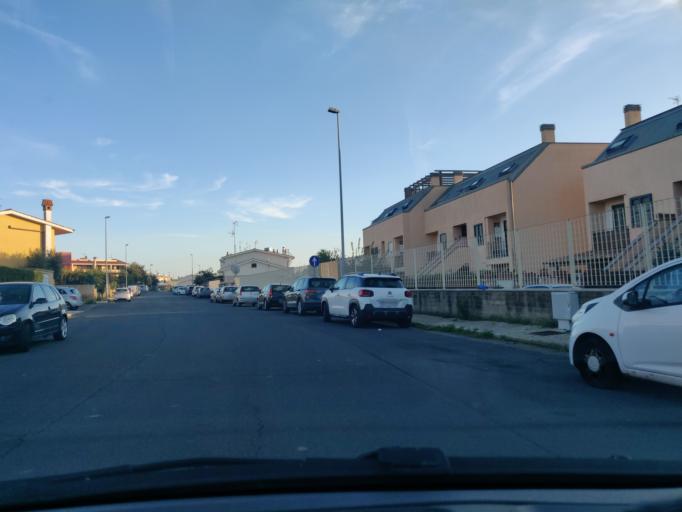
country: IT
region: Latium
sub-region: Citta metropolitana di Roma Capitale
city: Civitavecchia
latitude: 42.0651
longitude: 11.8170
